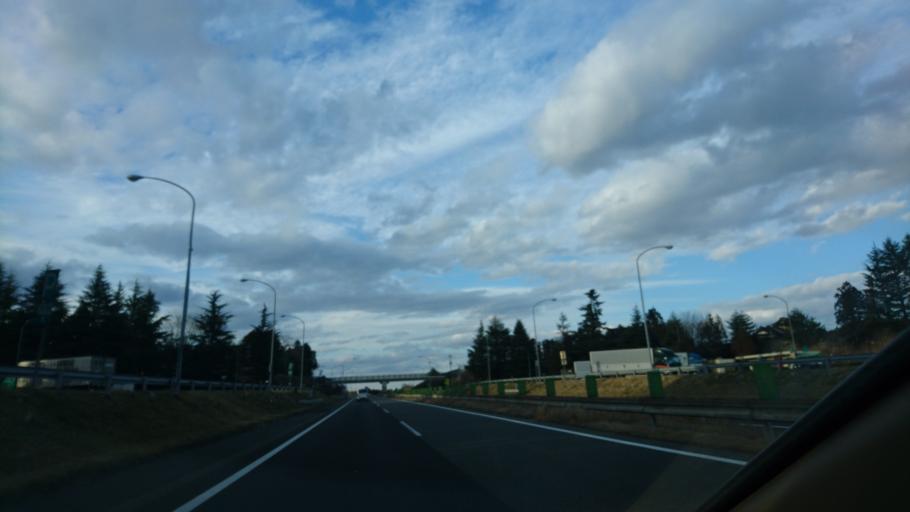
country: JP
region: Iwate
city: Ichinoseki
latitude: 38.7467
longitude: 141.0466
